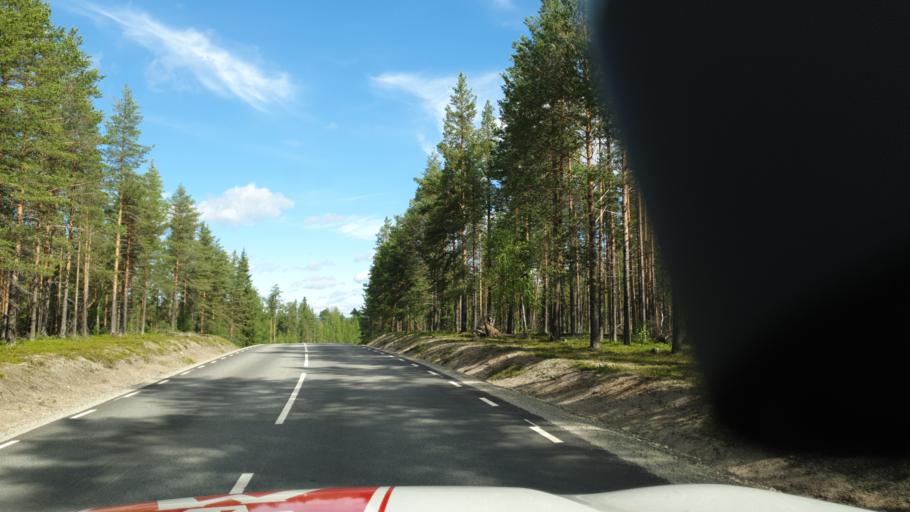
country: SE
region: Vaesterbotten
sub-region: Norsjo Kommun
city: Norsjoe
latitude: 64.6339
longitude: 19.2885
